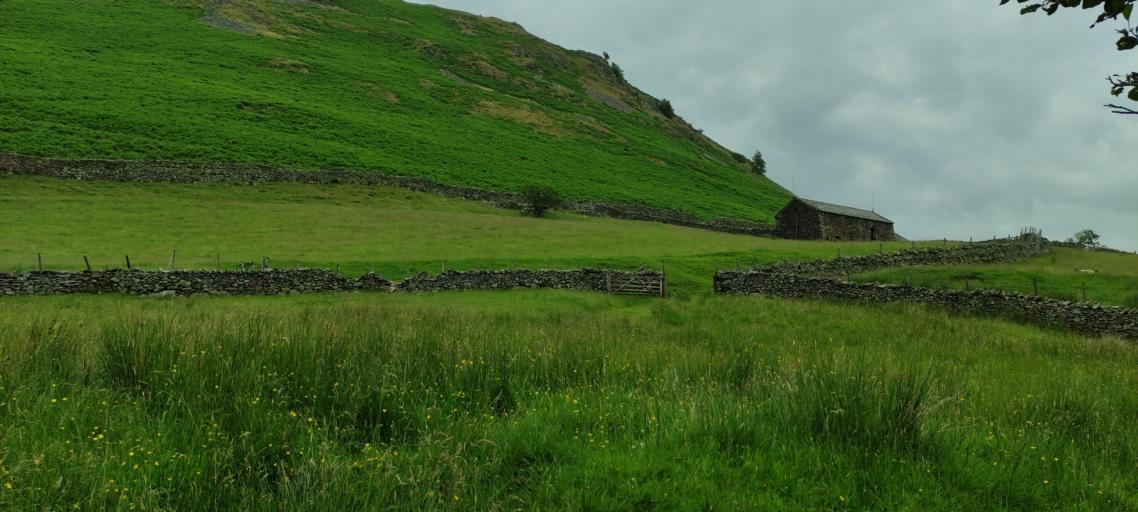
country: GB
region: England
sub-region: Cumbria
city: Ambleside
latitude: 54.5588
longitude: -2.8893
